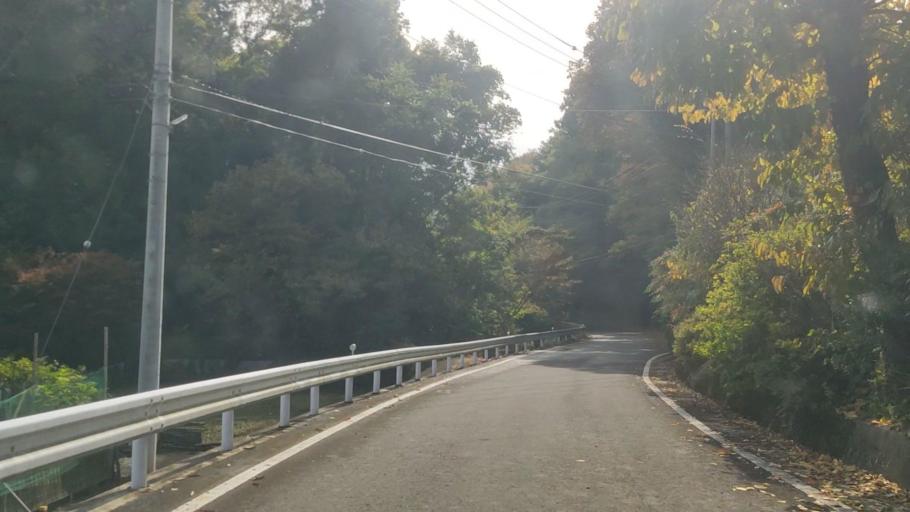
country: JP
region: Yamanashi
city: Ryuo
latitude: 35.4485
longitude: 138.4490
